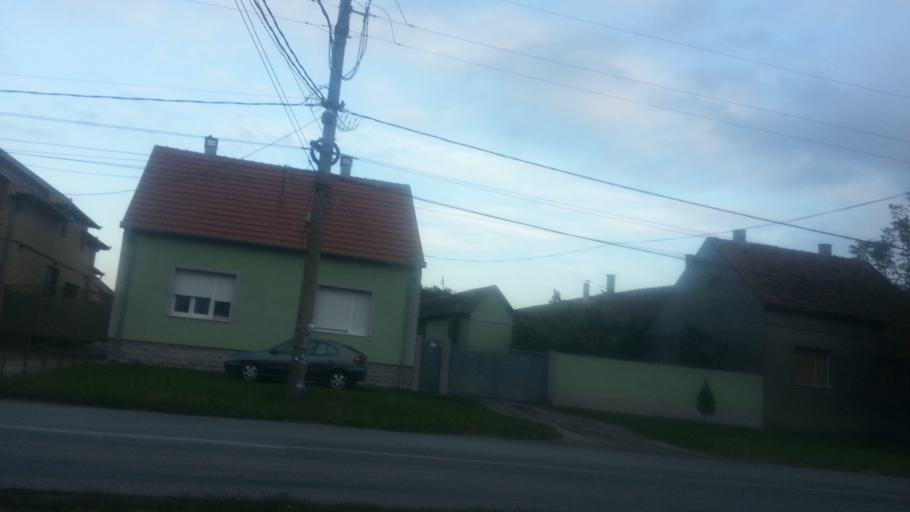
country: RS
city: Novi Banovci
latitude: 44.9122
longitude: 20.2812
